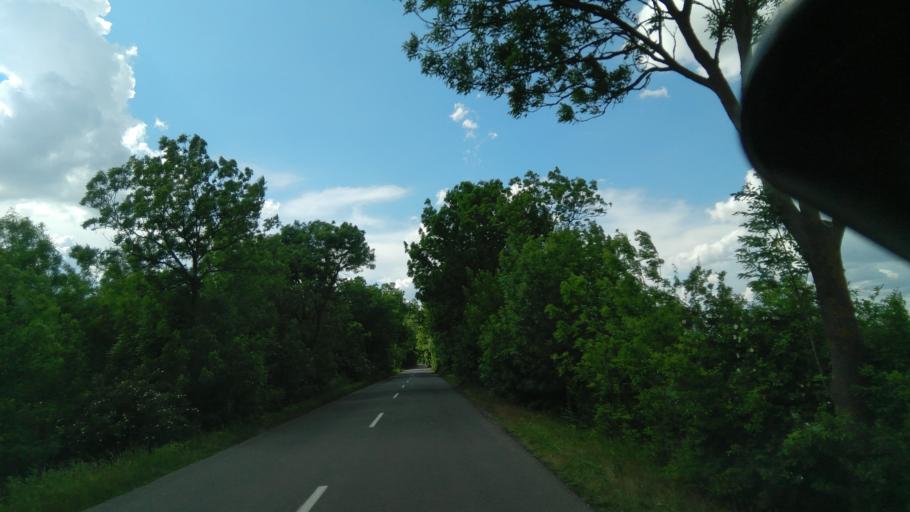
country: HU
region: Bekes
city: Bucsa
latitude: 47.1809
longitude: 21.0493
